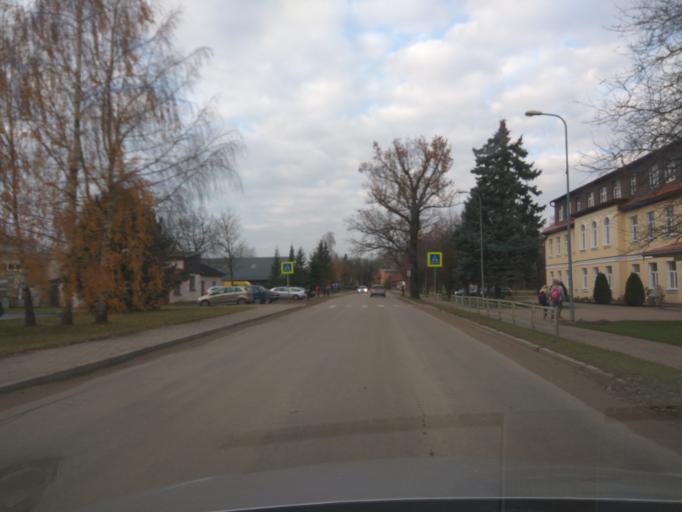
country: LV
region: Kuldigas Rajons
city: Kuldiga
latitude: 56.9622
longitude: 21.9834
